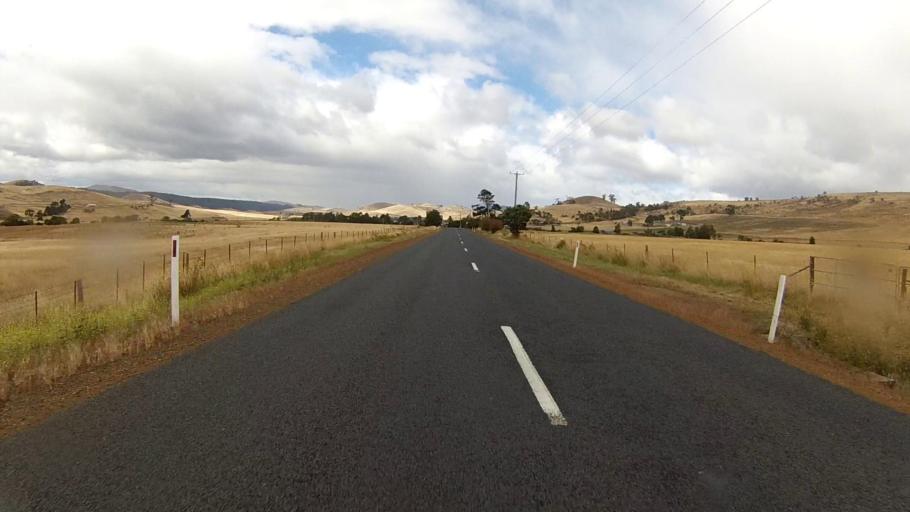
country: AU
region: Tasmania
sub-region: Brighton
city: Bridgewater
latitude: -42.5267
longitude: 147.3589
